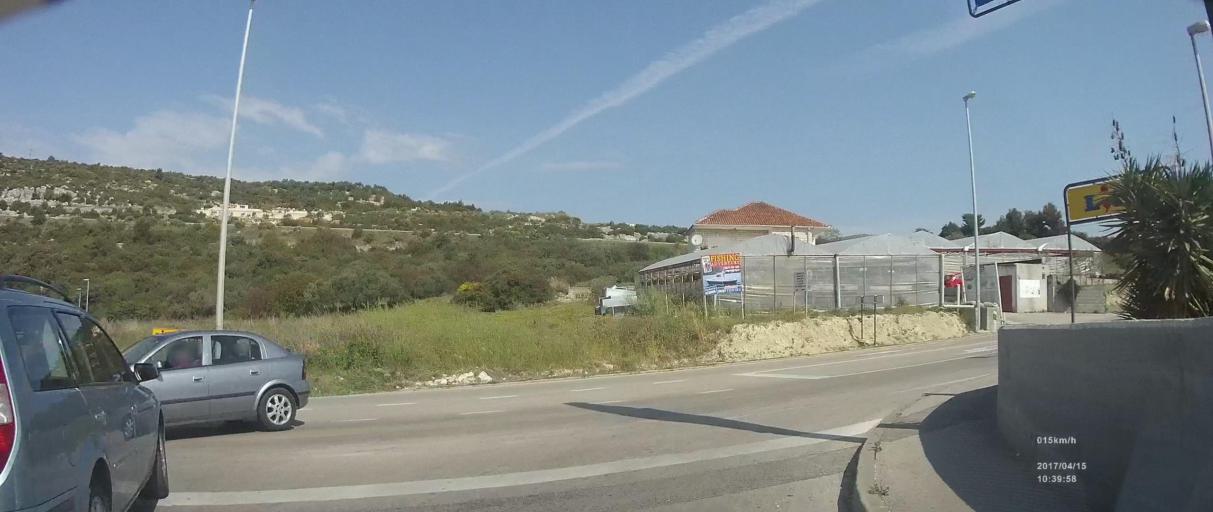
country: HR
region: Splitsko-Dalmatinska
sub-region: Grad Trogir
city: Trogir
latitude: 43.5333
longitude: 16.2820
